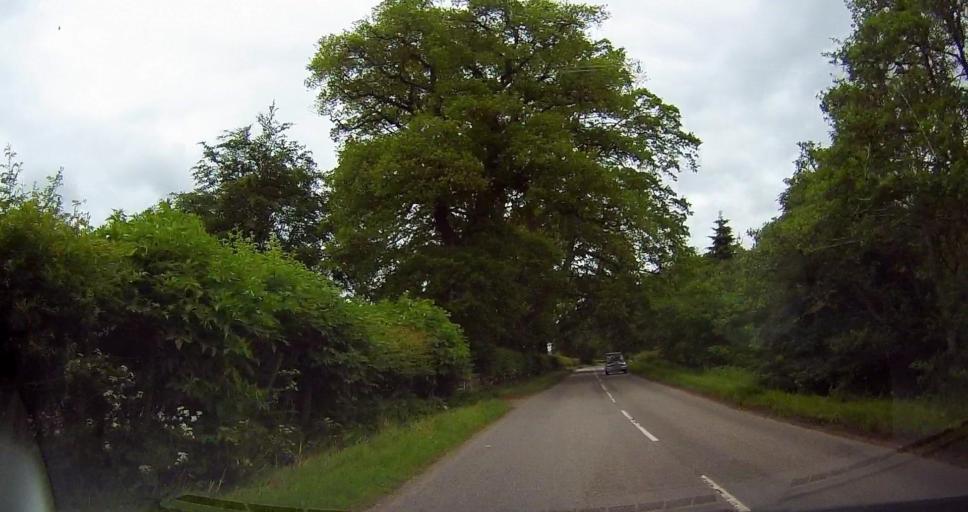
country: GB
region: Scotland
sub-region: Highland
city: Dornoch
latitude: 57.9768
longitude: -4.1063
